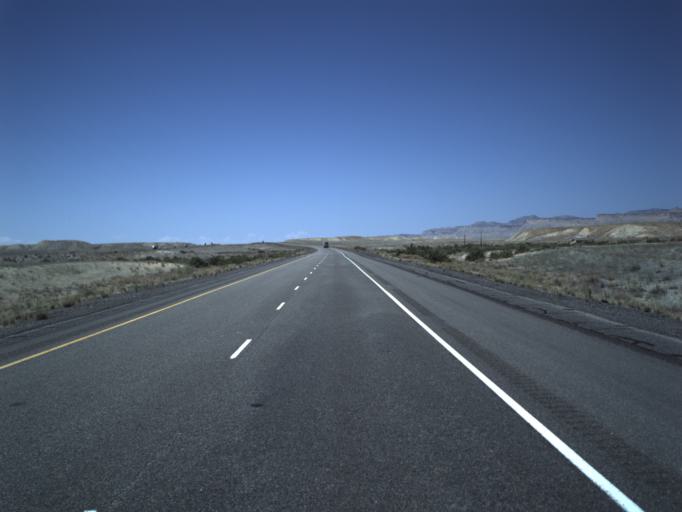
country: US
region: Utah
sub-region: Grand County
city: Moab
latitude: 38.9418
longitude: -109.5197
